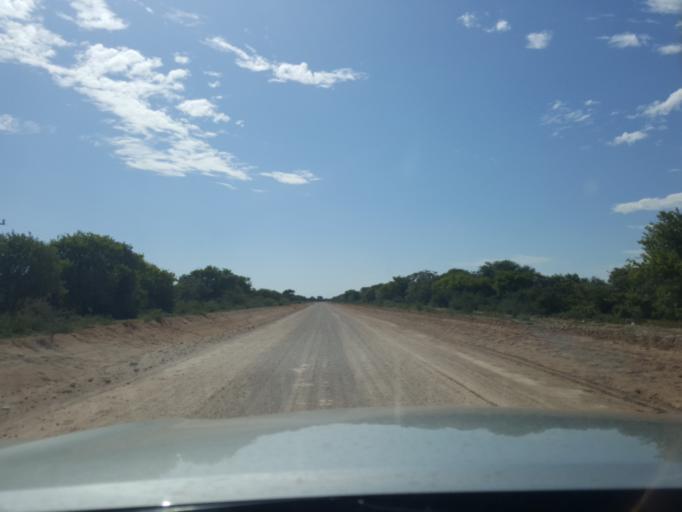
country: BW
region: Kweneng
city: Khudumelapye
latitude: -23.7959
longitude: 24.7961
